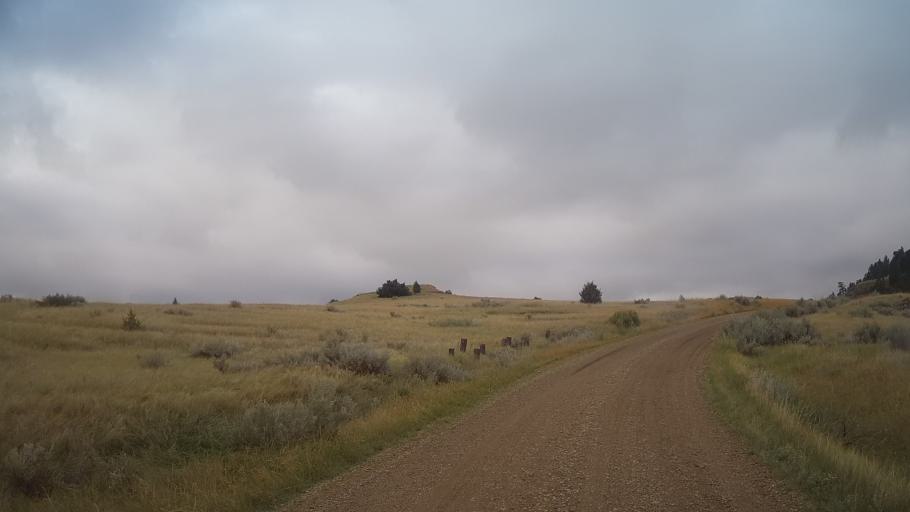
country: US
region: Montana
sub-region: Dawson County
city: Glendive
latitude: 47.0548
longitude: -104.6713
